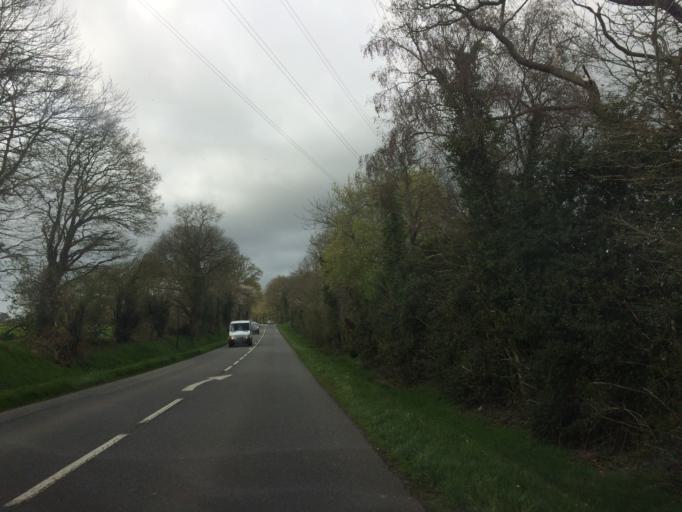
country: FR
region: Brittany
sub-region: Departement du Morbihan
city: Pluherlin
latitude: 47.6773
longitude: -2.3818
